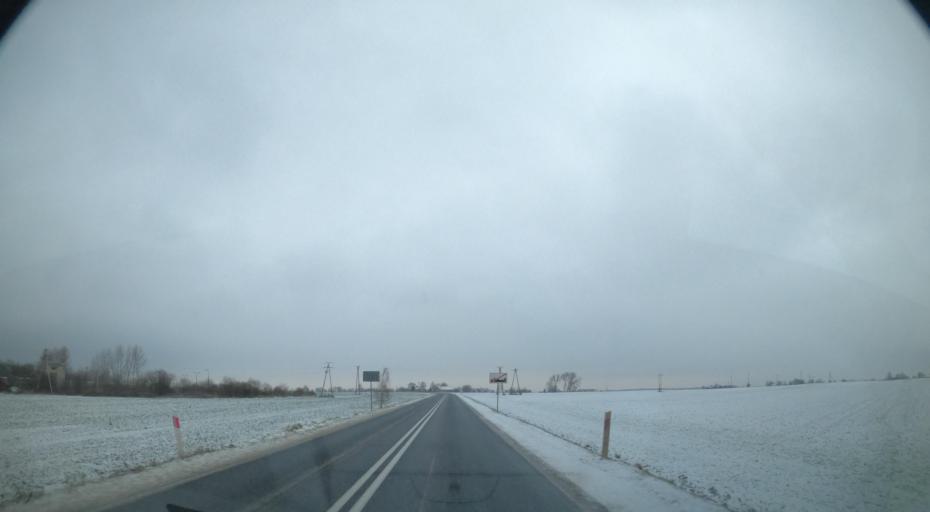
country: PL
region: Masovian Voivodeship
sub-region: Powiat plocki
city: Nowy Duninow
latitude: 52.6160
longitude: 19.4582
